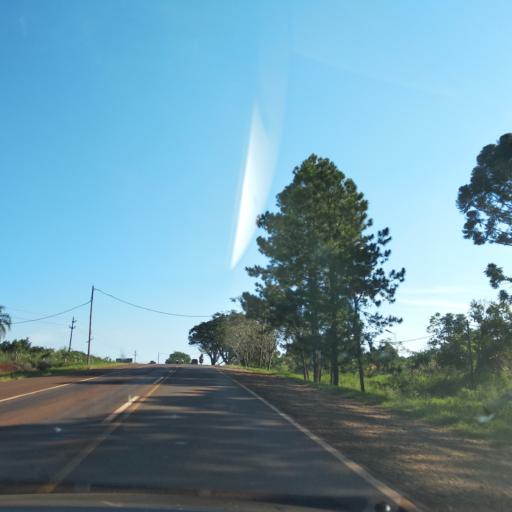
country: AR
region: Misiones
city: Jardin America
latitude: -27.0593
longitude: -55.2586
